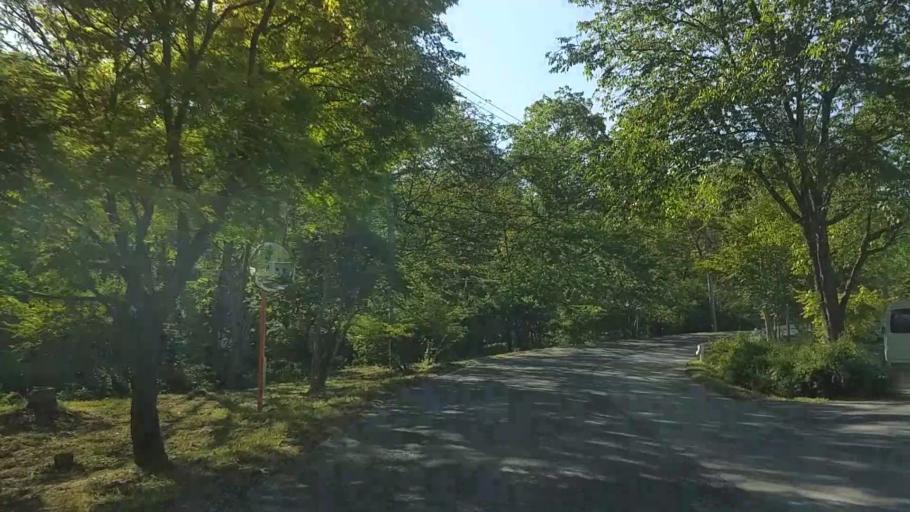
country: JP
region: Yamanashi
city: Nirasaki
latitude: 35.8870
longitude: 138.3567
